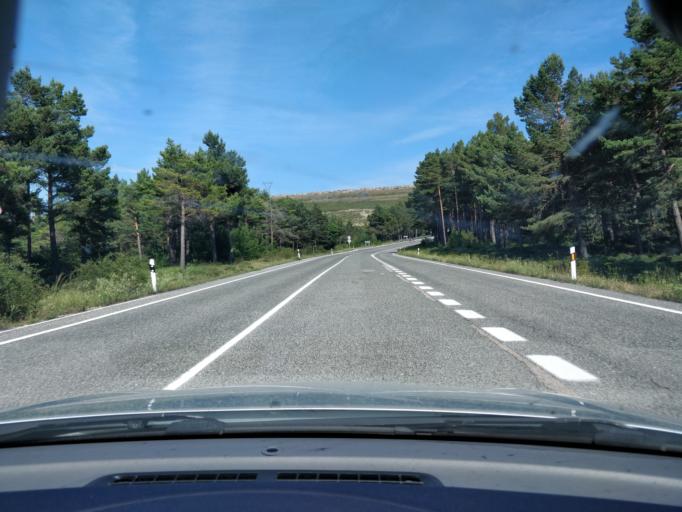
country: ES
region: Castille and Leon
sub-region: Provincia de Burgos
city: Espinosa de los Monteros
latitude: 42.9421
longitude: -3.6757
